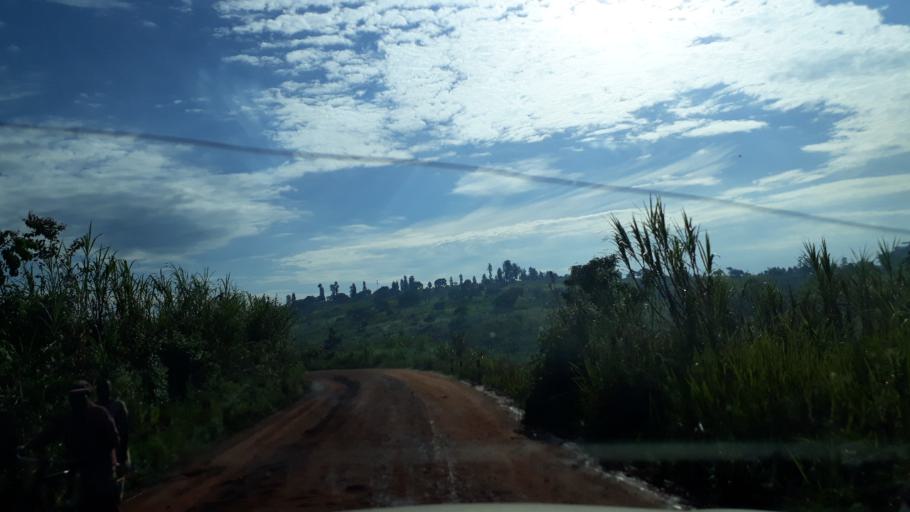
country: UG
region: Northern Region
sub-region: Zombo District
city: Paidha
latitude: 2.2594
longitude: 30.9369
